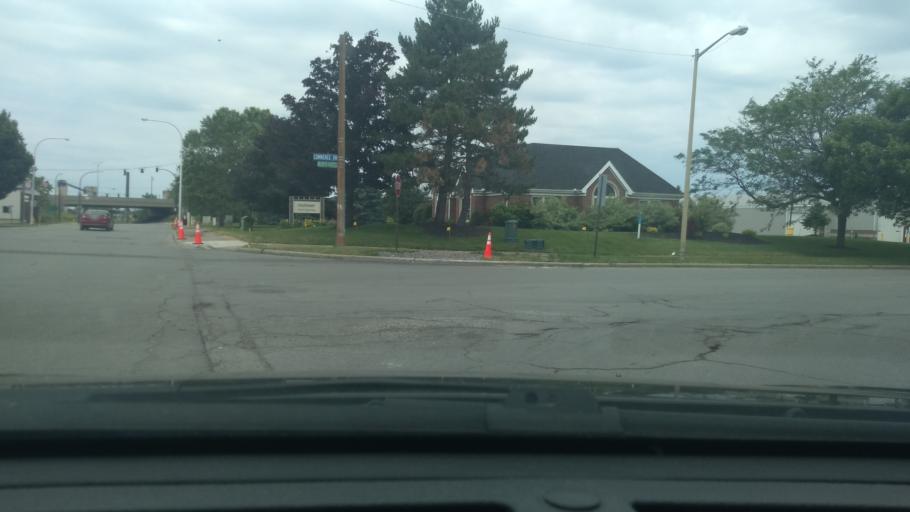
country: US
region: New York
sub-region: Erie County
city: Lackawanna
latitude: 42.8277
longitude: -78.8482
